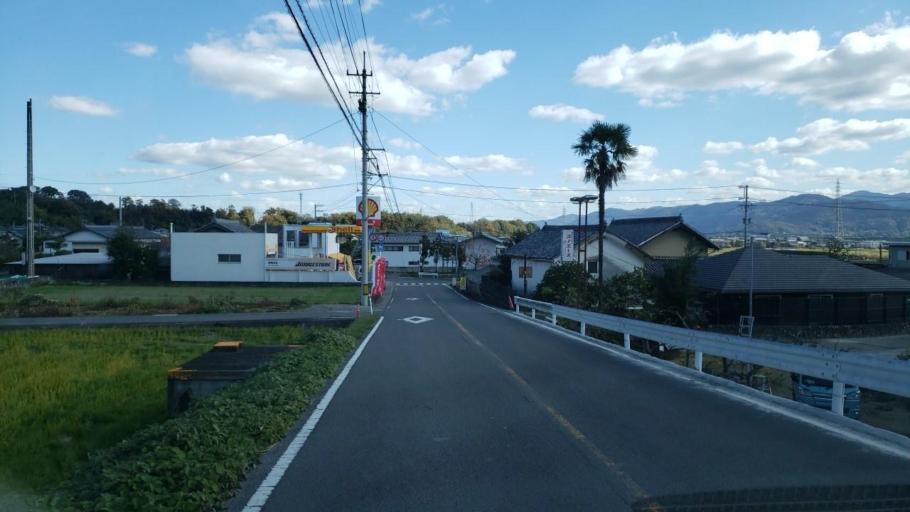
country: JP
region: Tokushima
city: Wakimachi
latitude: 34.0811
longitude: 134.2061
